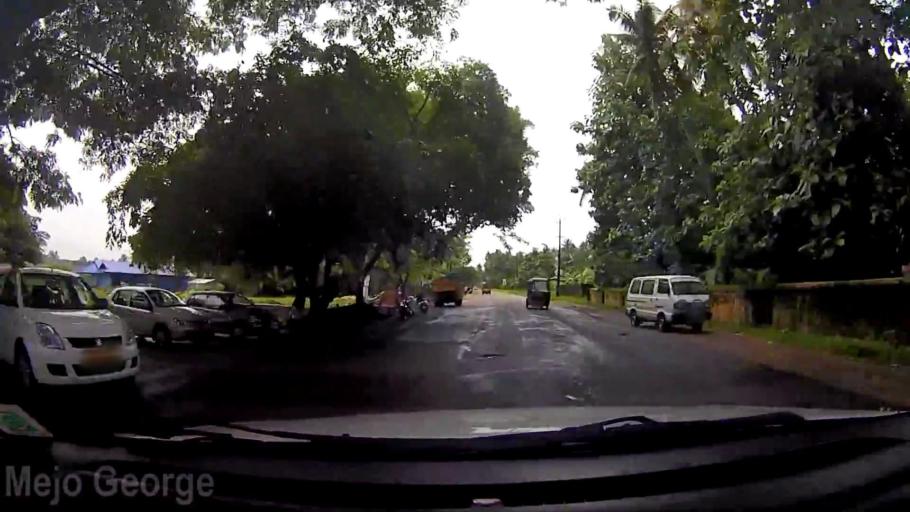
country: IN
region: Kerala
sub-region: Thrissur District
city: Kizhake Chalakudi
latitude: 10.3311
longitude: 76.3154
